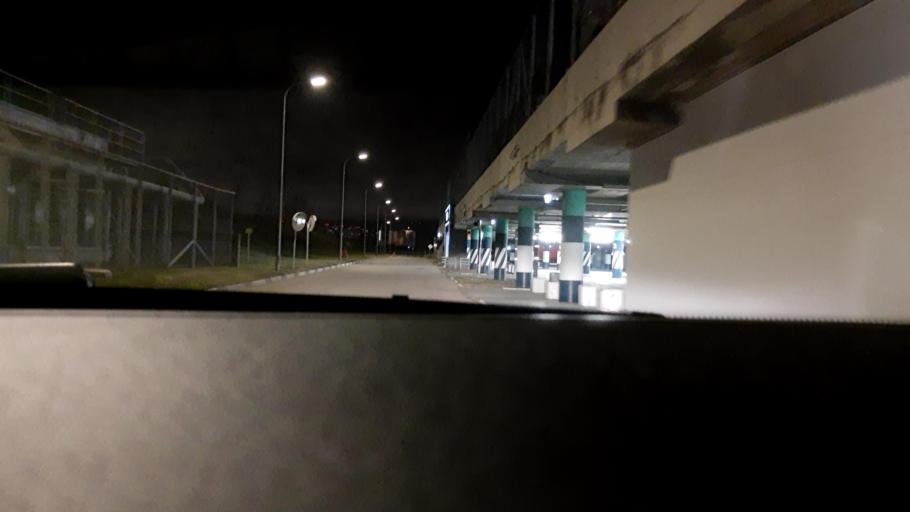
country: RU
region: Nizjnij Novgorod
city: Afonino
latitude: 56.2253
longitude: 44.0680
